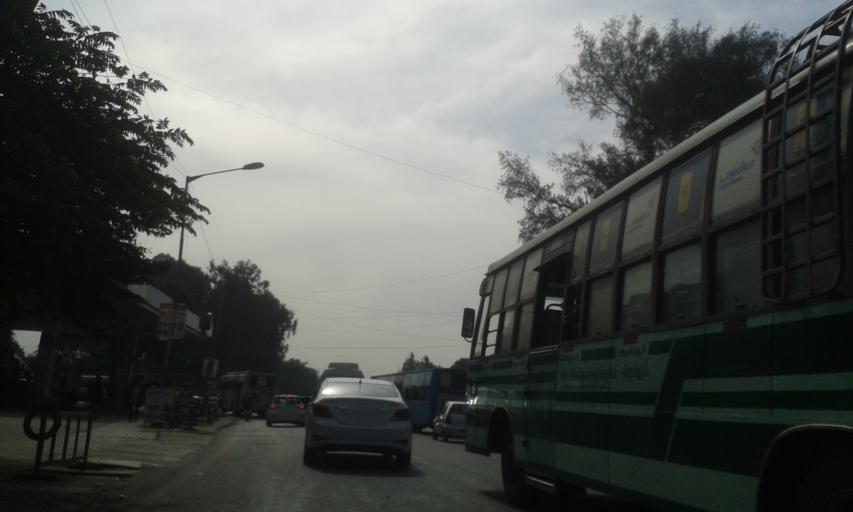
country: IN
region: Karnataka
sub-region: Bangalore Urban
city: Bangalore
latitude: 12.9304
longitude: 77.6147
